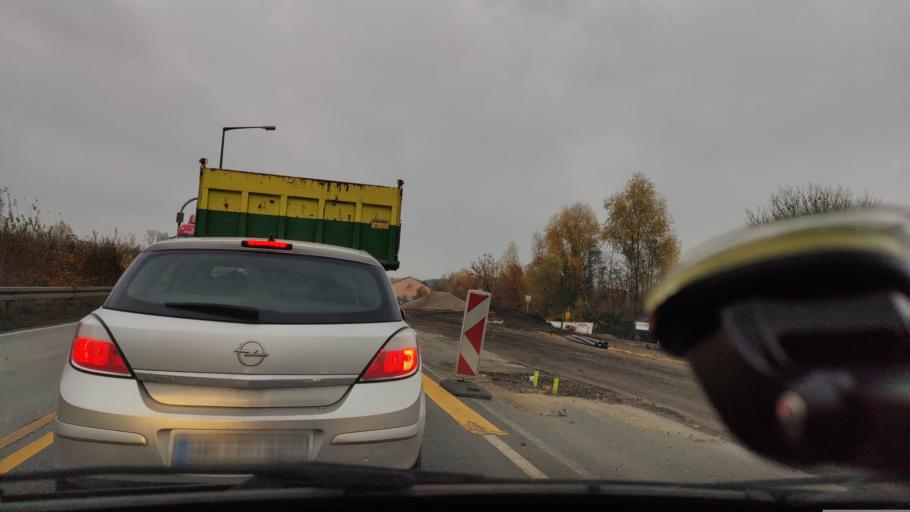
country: DE
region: North Rhine-Westphalia
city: Lunen
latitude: 51.6005
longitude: 7.4890
